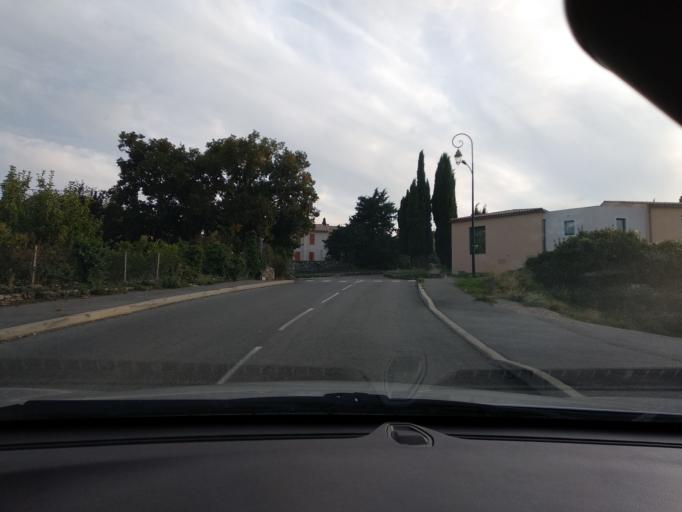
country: FR
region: Provence-Alpes-Cote d'Azur
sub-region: Departement des Alpes-Maritimes
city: Saint-Cezaire-sur-Siagne
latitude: 43.6501
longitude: 6.7969
